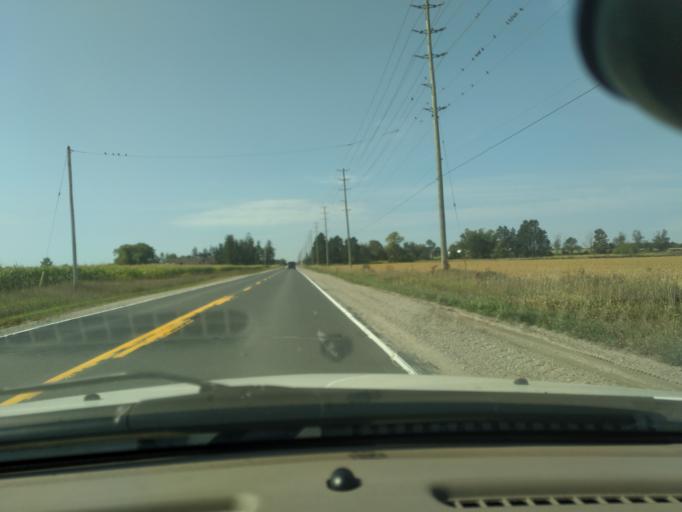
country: CA
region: Ontario
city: Innisfil
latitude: 44.2797
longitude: -79.7038
